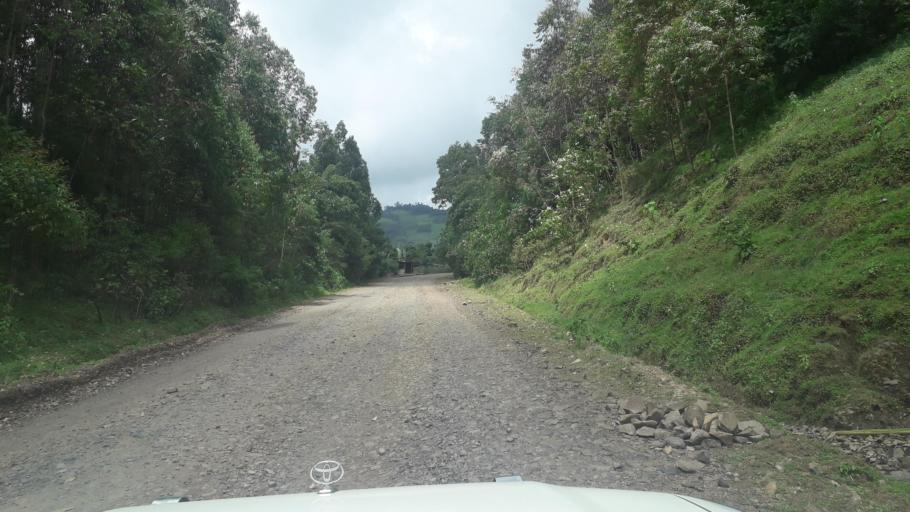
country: ET
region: Oromiya
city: Jima
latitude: 7.4320
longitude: 36.8748
